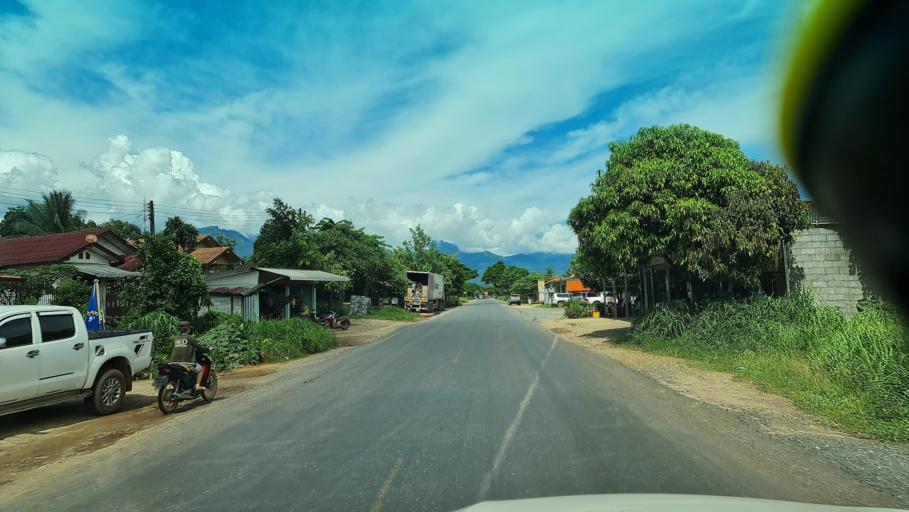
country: LA
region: Bolikhamxai
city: Pakkading
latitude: 18.2993
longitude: 104.0966
